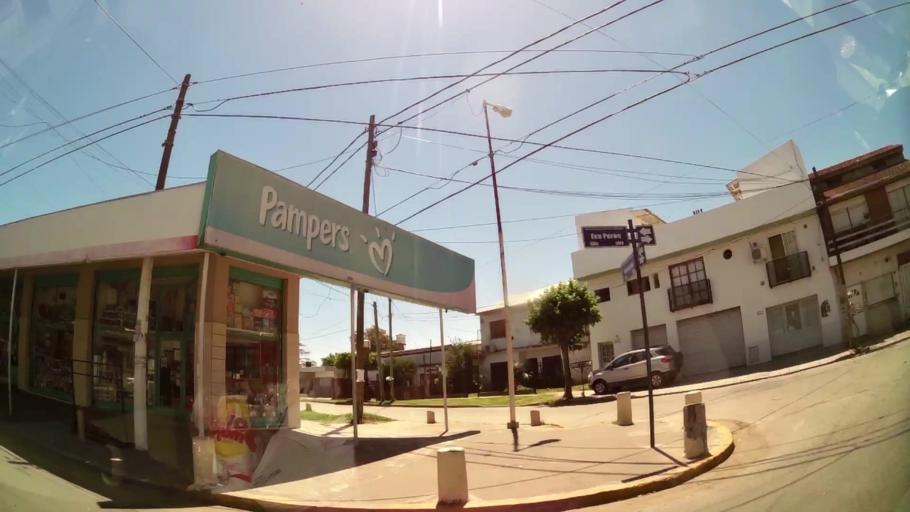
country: AR
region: Buenos Aires
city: Hurlingham
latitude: -34.4888
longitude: -58.6650
